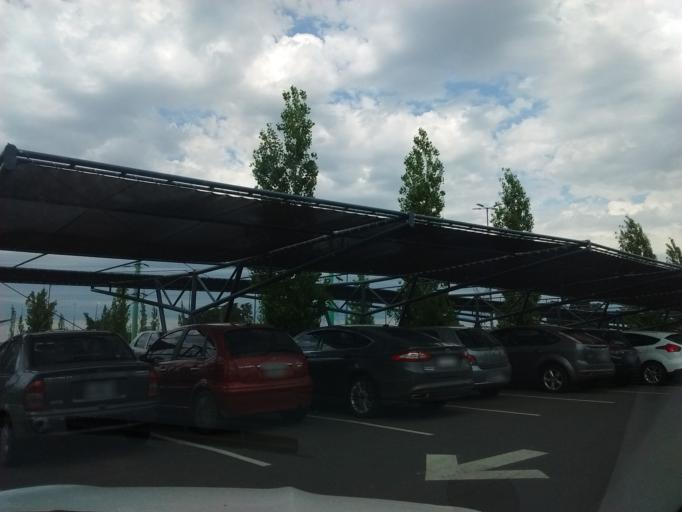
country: AR
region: Santa Fe
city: Granadero Baigorria
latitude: -32.9069
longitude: -60.7219
